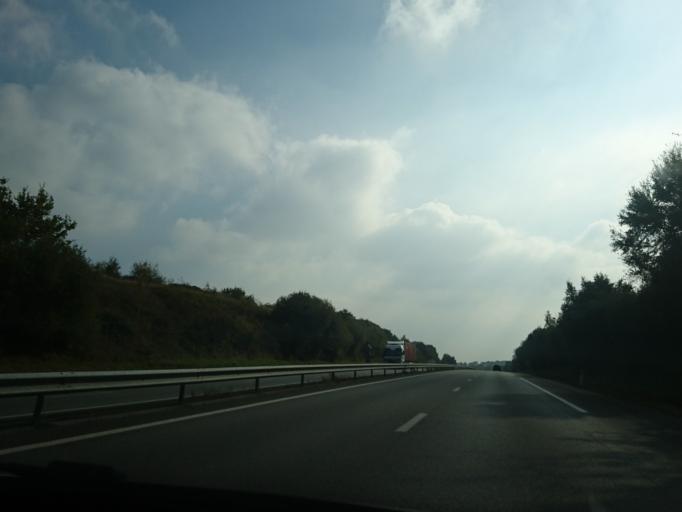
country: FR
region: Brittany
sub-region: Departement d'Ille-et-Vilaine
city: La Dominelais
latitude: 47.7524
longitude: -1.7150
